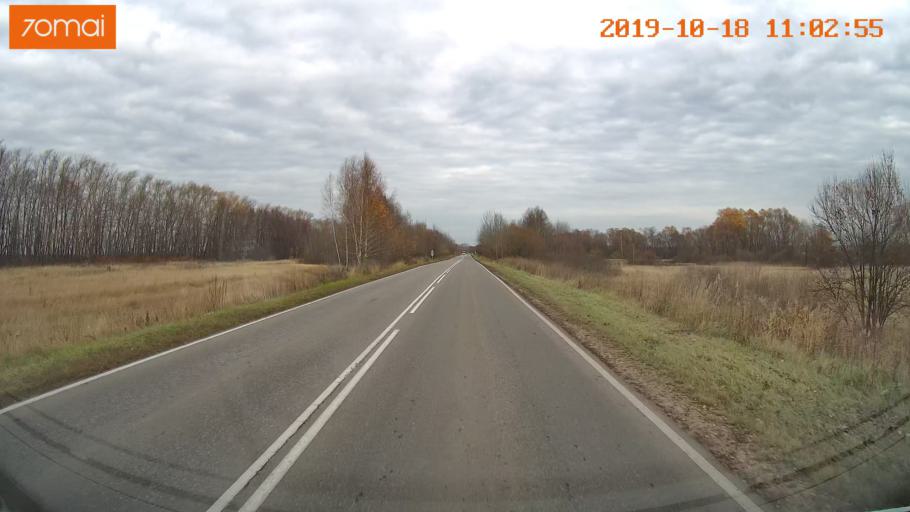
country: RU
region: Tula
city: Yepifan'
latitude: 53.8723
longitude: 38.5443
